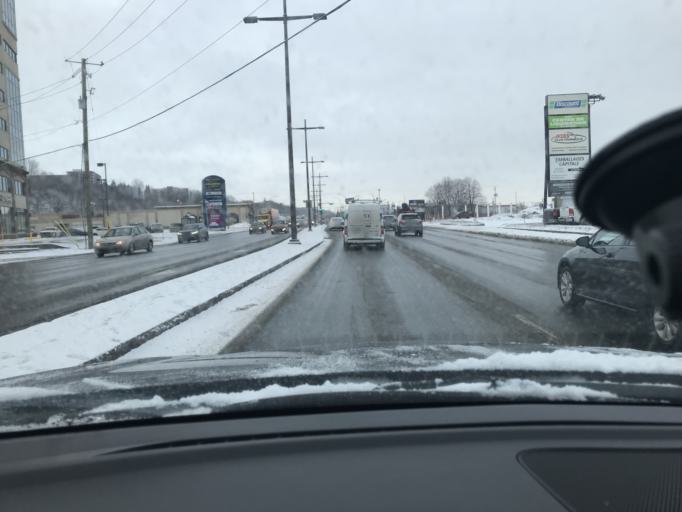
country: CA
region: Quebec
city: Quebec
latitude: 46.7995
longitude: -71.2550
